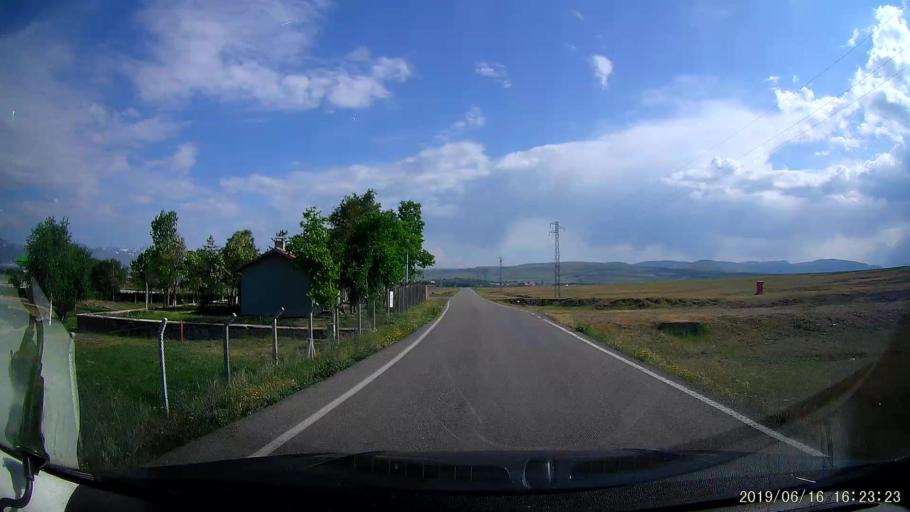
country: TR
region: Erzurum
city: Ilica
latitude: 39.9787
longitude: 41.1065
